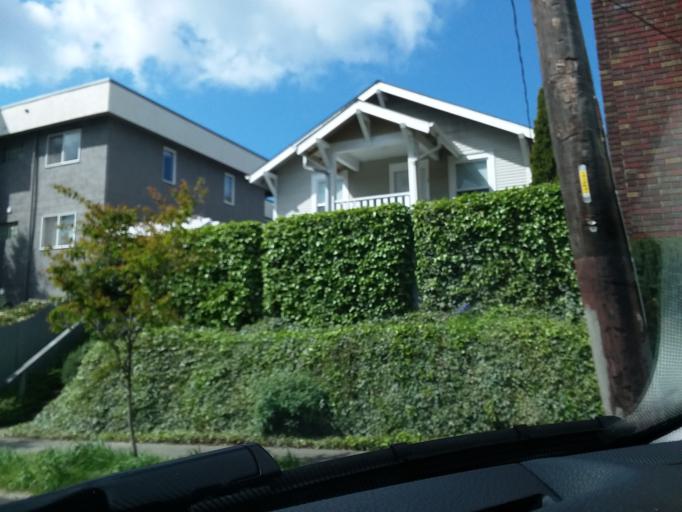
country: US
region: Washington
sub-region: King County
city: Seattle
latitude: 47.6375
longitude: -122.3260
